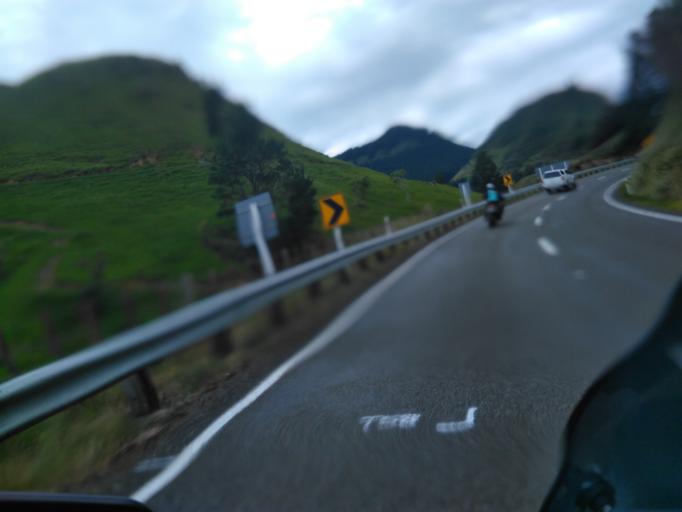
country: NZ
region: Bay of Plenty
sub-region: Opotiki District
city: Opotiki
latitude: -38.3750
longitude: 177.4663
